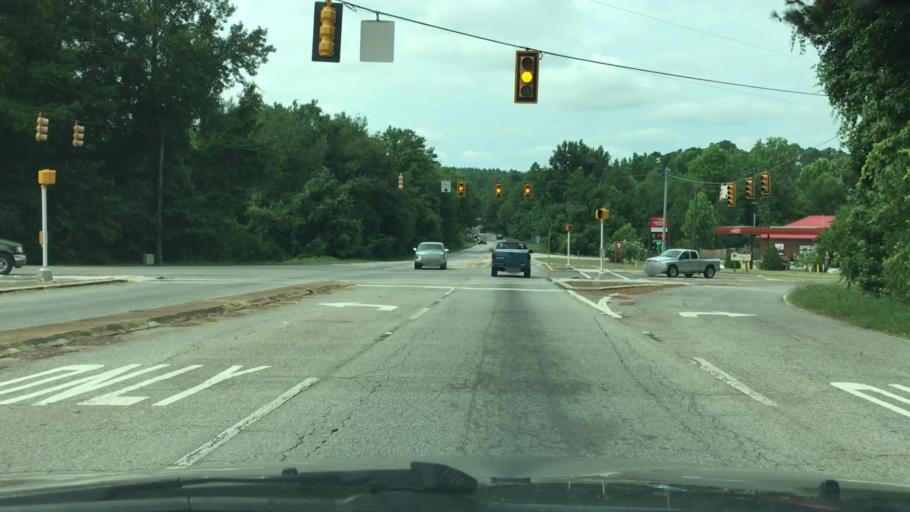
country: US
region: South Carolina
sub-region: Aiken County
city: Warrenville
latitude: 33.5589
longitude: -81.7787
